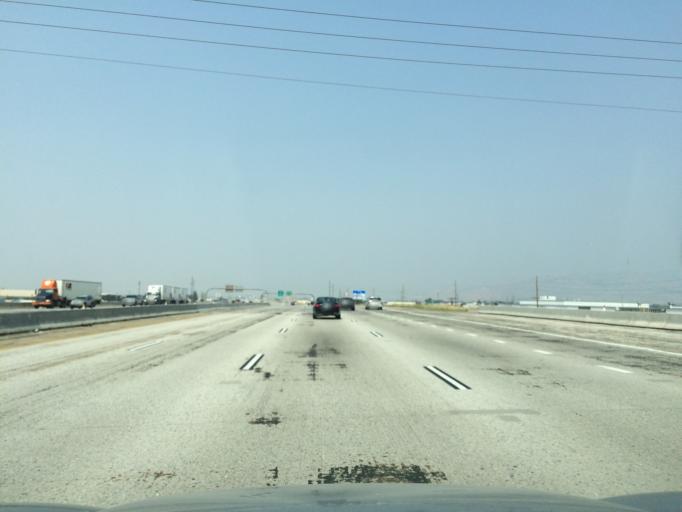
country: US
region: Utah
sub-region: Salt Lake County
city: South Salt Lake
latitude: 40.7326
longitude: -111.9495
